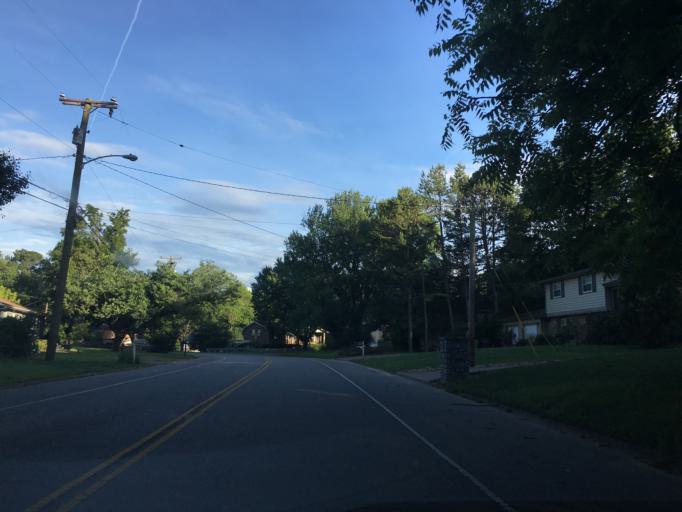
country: US
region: Tennessee
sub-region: Davidson County
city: Oak Hill
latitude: 36.0639
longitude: -86.7365
